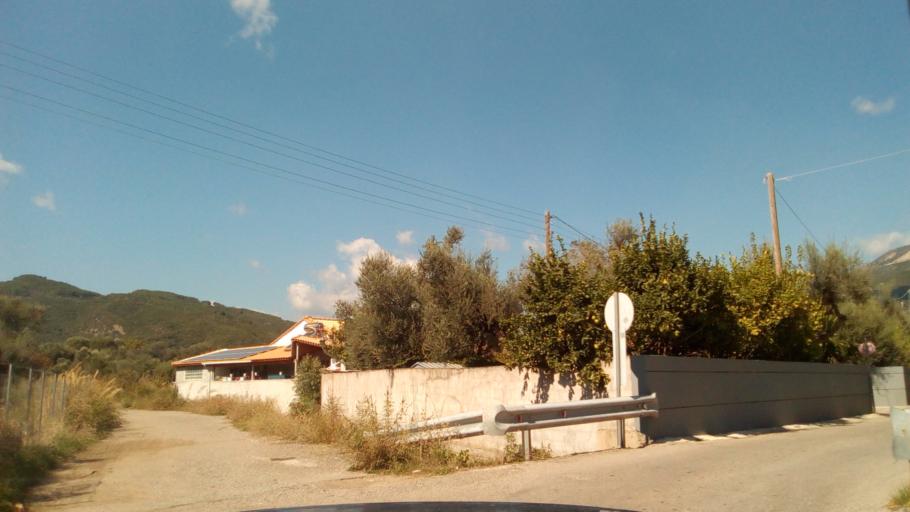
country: GR
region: West Greece
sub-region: Nomos Aitolias kai Akarnanias
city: Nafpaktos
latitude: 38.3957
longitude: 21.7978
